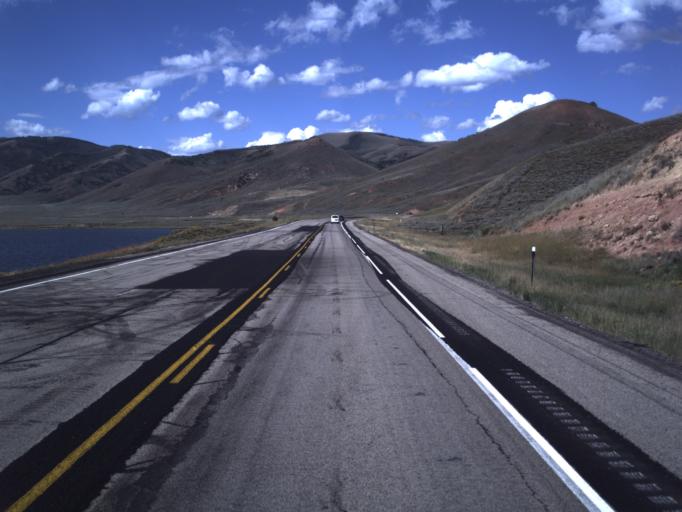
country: US
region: Utah
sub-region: Wasatch County
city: Heber
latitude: 40.2042
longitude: -111.1047
